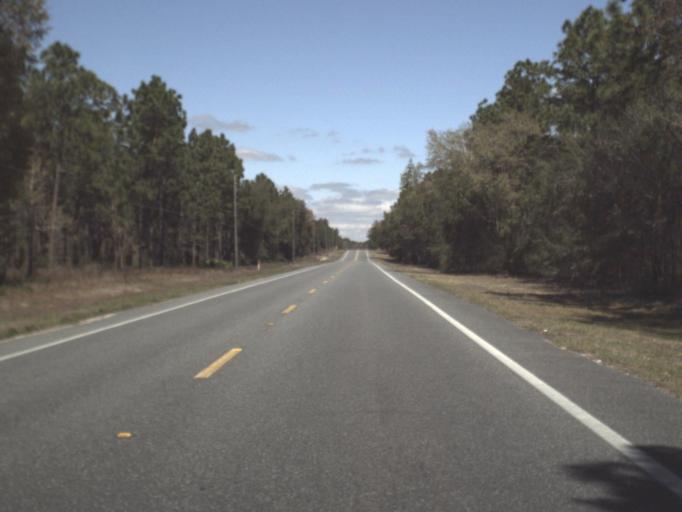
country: US
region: Florida
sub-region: Wakulla County
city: Crawfordville
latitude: 30.0616
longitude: -84.3886
